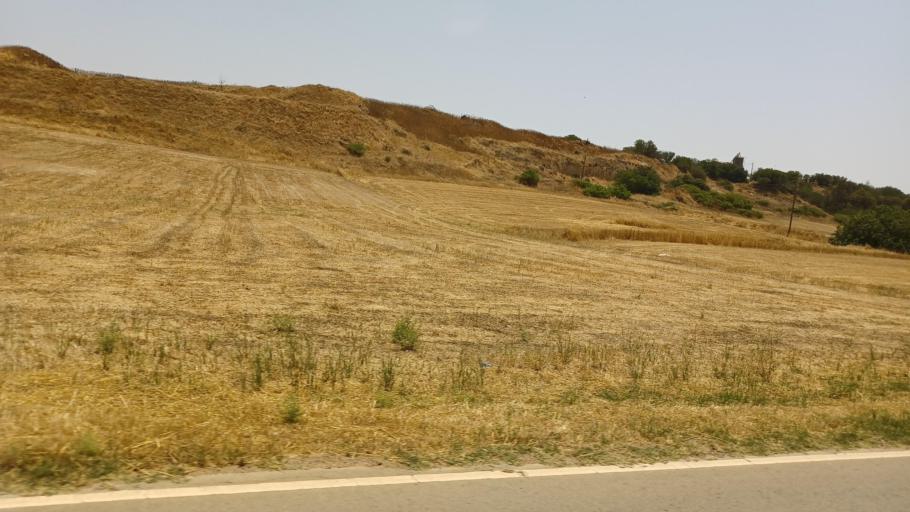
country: CY
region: Ammochostos
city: Avgorou
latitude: 35.0543
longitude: 33.8374
